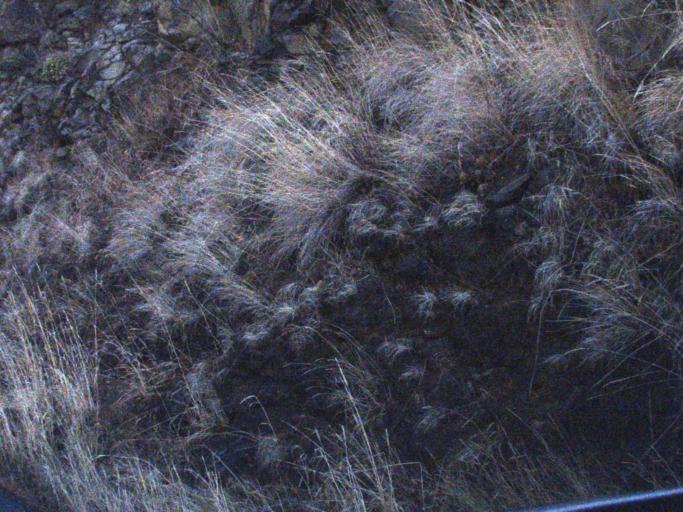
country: US
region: Washington
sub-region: Asotin County
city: Asotin
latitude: 46.0841
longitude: -117.1817
